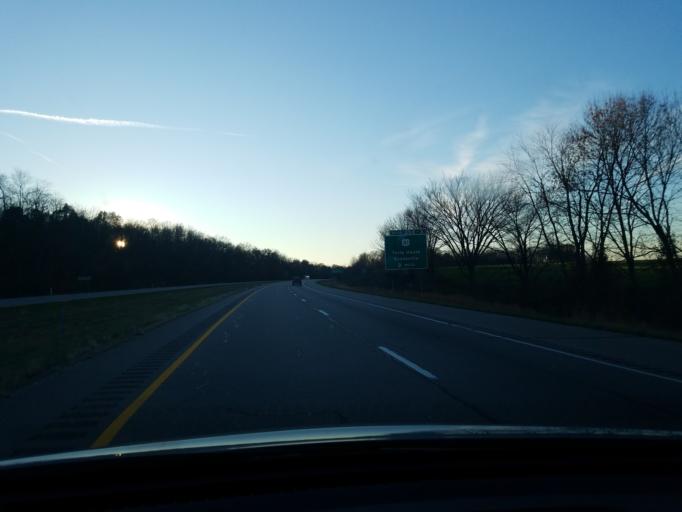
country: US
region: Indiana
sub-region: Gibson County
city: Haubstadt
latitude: 38.1657
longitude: -87.5049
